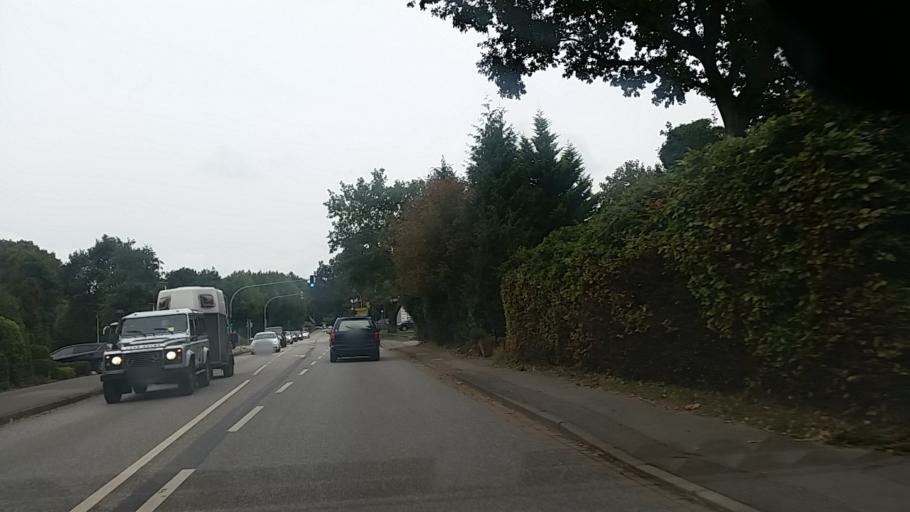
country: DE
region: Schleswig-Holstein
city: Kayhude
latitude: 53.7520
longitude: 10.1273
